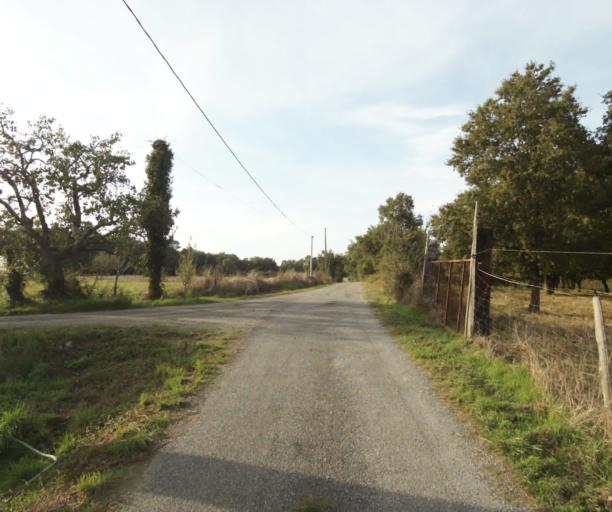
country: FR
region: Midi-Pyrenees
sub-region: Departement du Tarn-et-Garonne
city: Campsas
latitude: 43.8849
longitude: 1.3163
